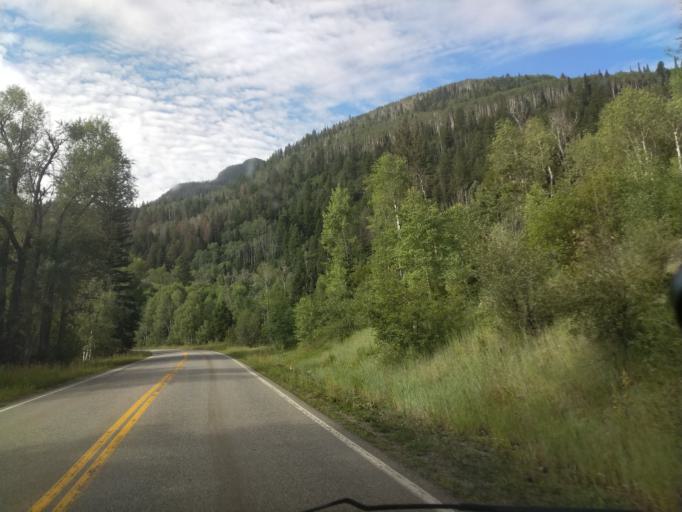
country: US
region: Colorado
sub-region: Garfield County
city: Carbondale
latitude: 39.0955
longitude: -107.2570
